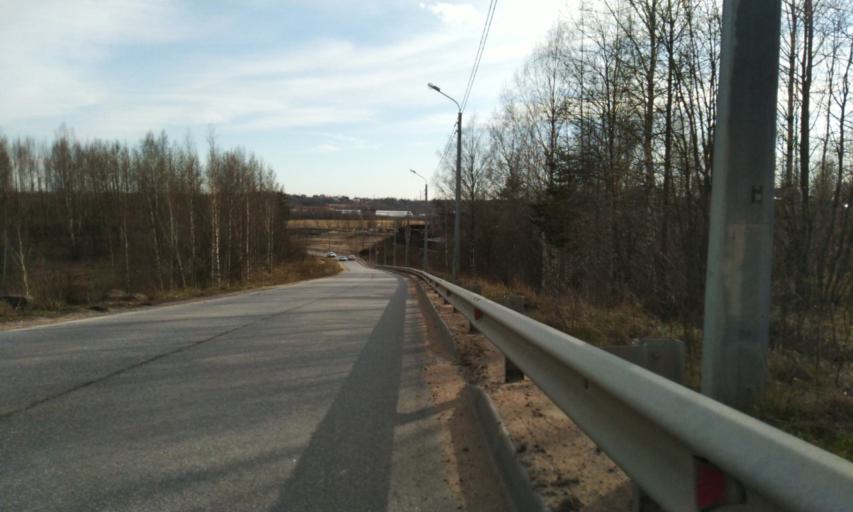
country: RU
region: Leningrad
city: Bugry
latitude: 60.1168
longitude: 30.4261
